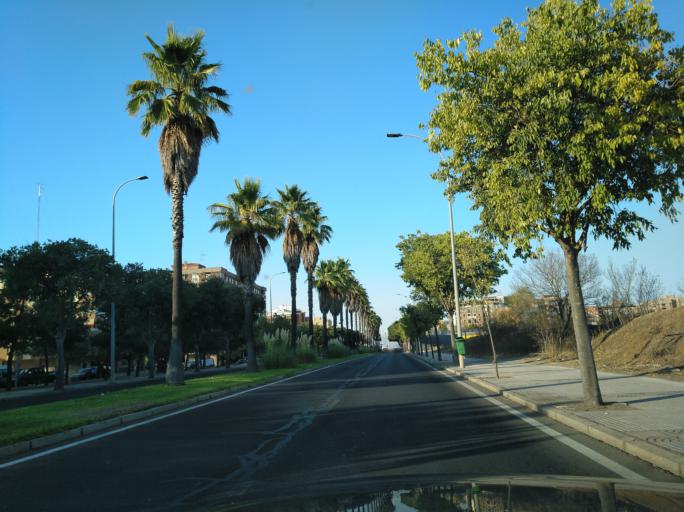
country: ES
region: Extremadura
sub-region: Provincia de Badajoz
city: Badajoz
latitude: 38.8631
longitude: -6.9845
